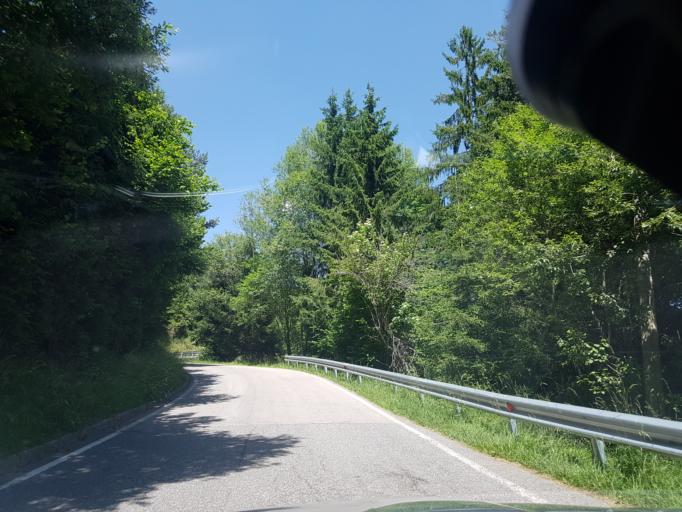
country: IT
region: Trentino-Alto Adige
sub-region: Bolzano
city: Villandro - Villanders
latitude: 46.6339
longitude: 11.5268
